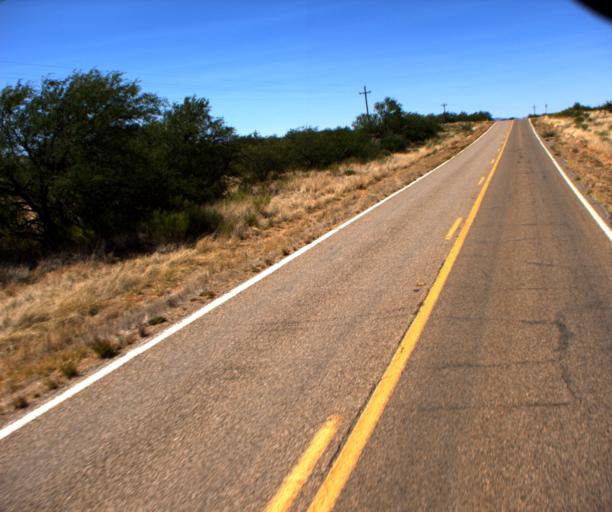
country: US
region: Arizona
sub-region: Santa Cruz County
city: Tubac
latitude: 31.5070
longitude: -111.5458
